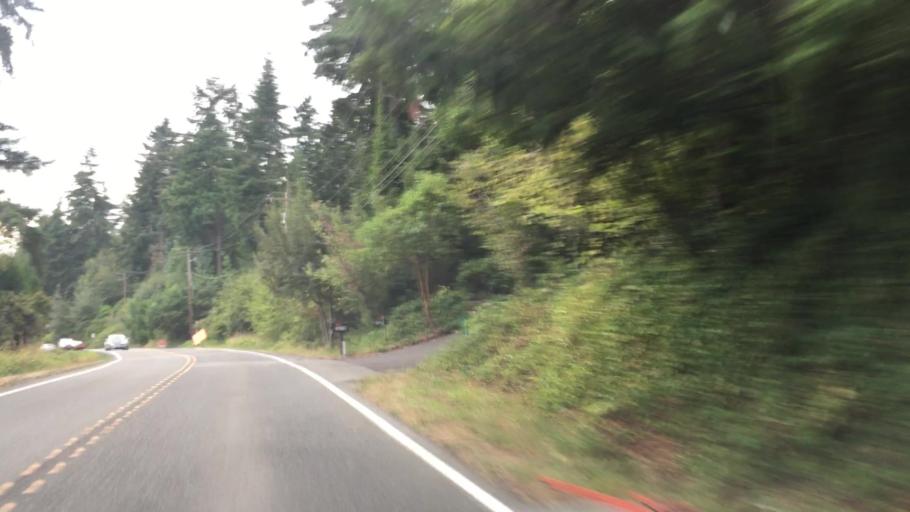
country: US
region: Washington
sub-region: King County
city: West Lake Sammamish
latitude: 47.5798
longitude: -122.1166
